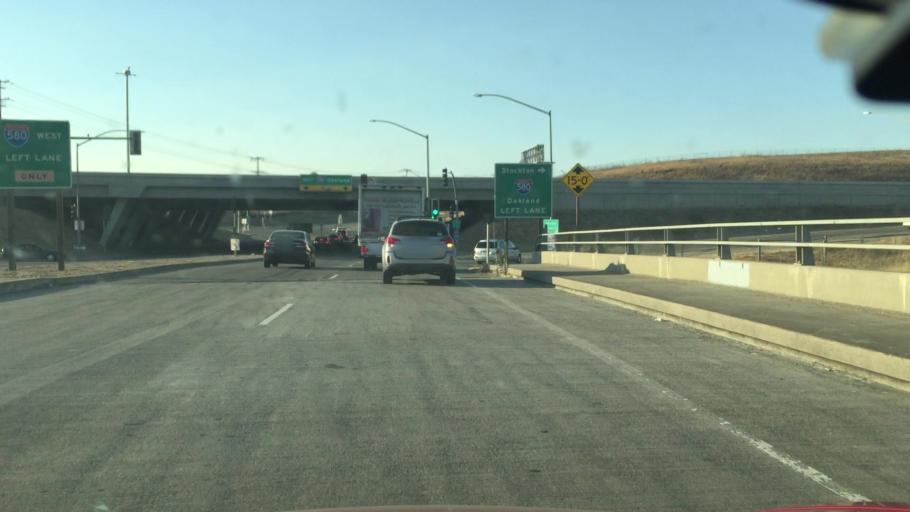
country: US
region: California
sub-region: Alameda County
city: Livermore
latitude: 37.6999
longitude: -121.7734
